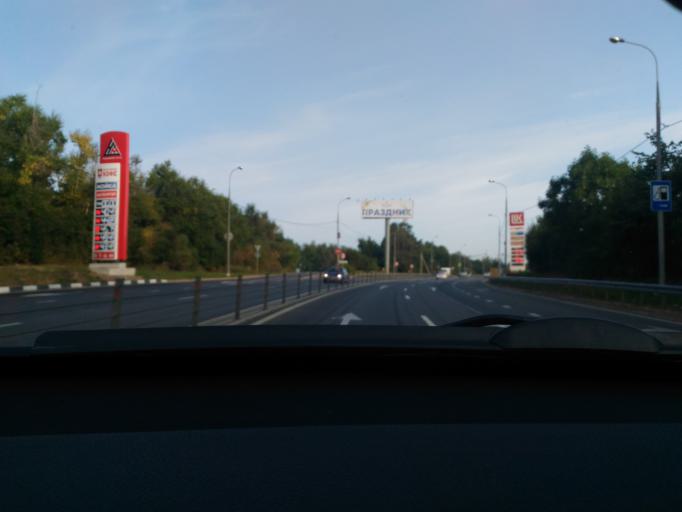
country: RU
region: Moskovskaya
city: Lugovaya
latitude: 56.0666
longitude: 37.5181
